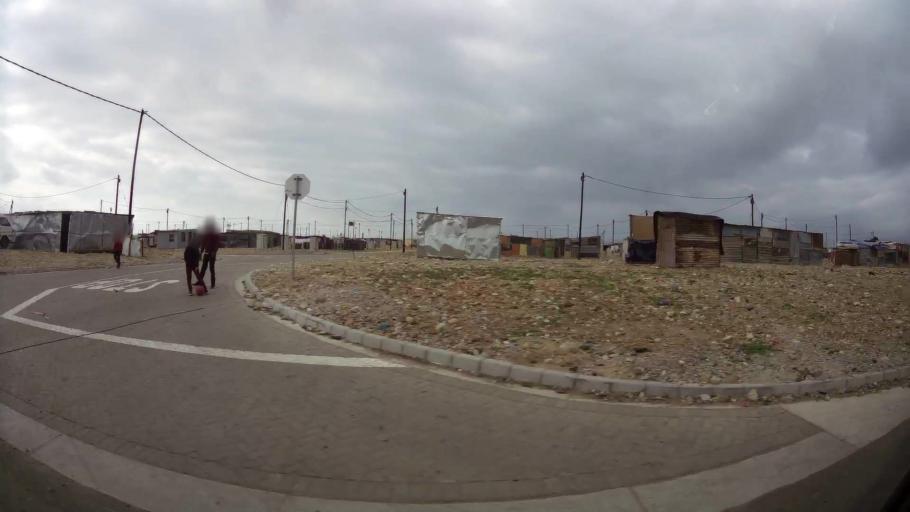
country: ZA
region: Eastern Cape
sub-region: Nelson Mandela Bay Metropolitan Municipality
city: Port Elizabeth
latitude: -33.8877
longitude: 25.6049
